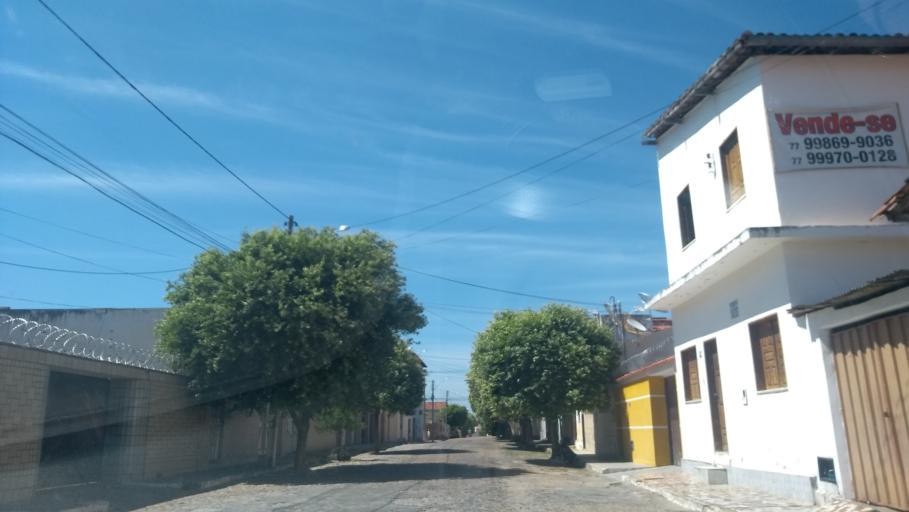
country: BR
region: Bahia
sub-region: Brumado
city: Brumado
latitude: -14.2058
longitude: -41.6668
